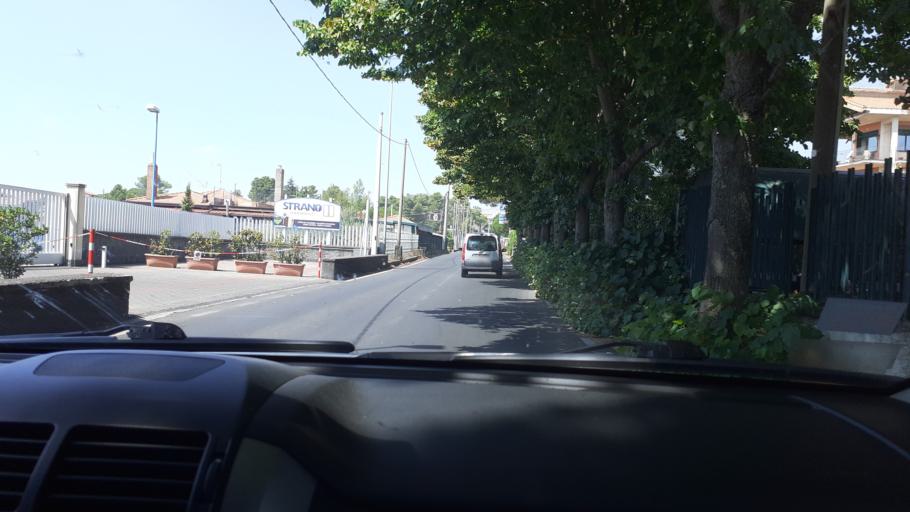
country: IT
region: Sicily
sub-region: Catania
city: Nicolosi
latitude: 37.6148
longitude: 15.0389
